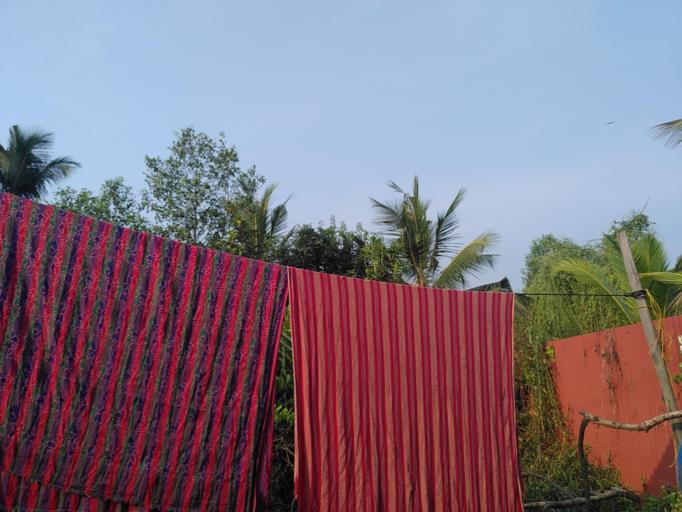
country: IN
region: Kerala
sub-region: Alappuzha
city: Arukutti
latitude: 9.9228
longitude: 76.3296
